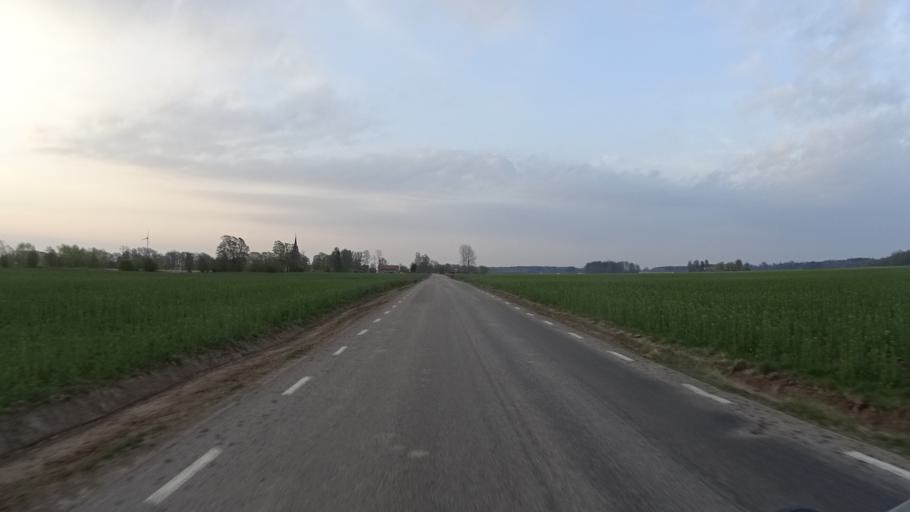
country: SE
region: Vaestra Goetaland
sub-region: Gotene Kommun
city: Kallby
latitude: 58.4770
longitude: 13.3222
